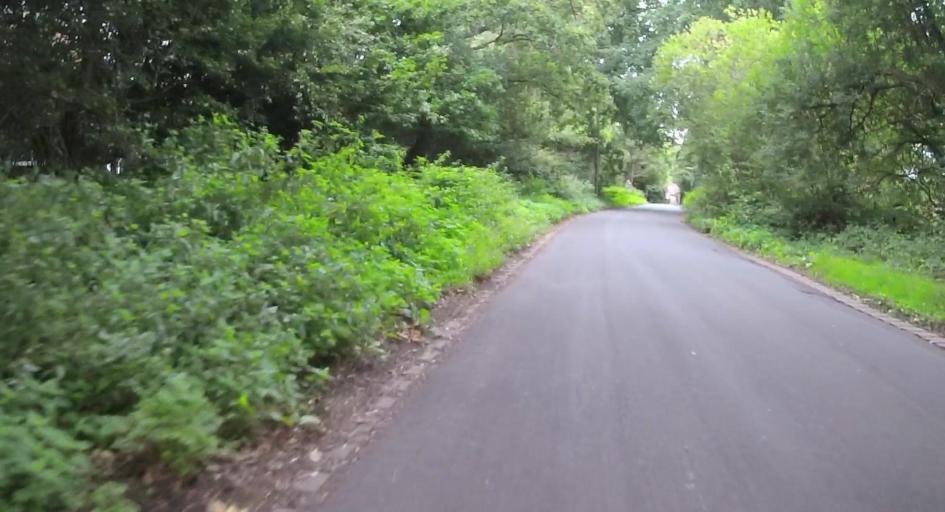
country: GB
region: England
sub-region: Surrey
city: Windlesham
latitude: 51.3363
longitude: -0.6486
